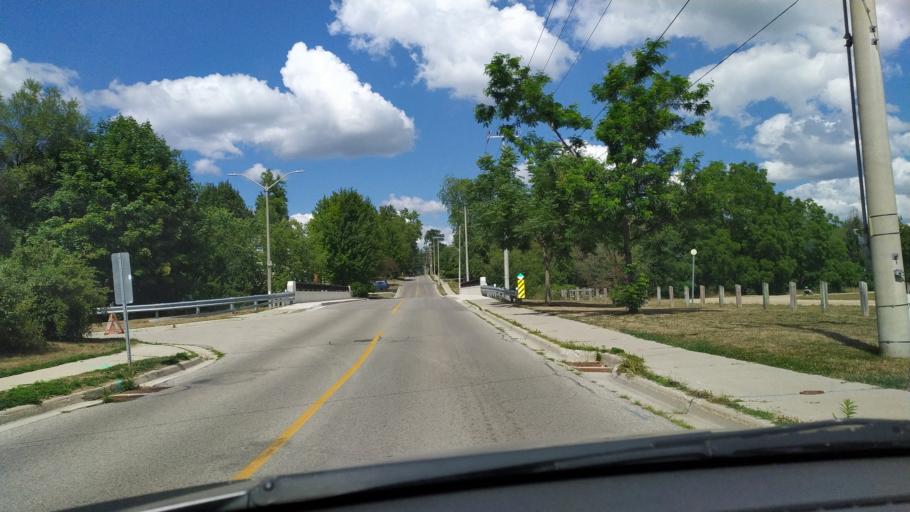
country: CA
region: Ontario
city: Stratford
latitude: 43.3713
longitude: -80.9906
